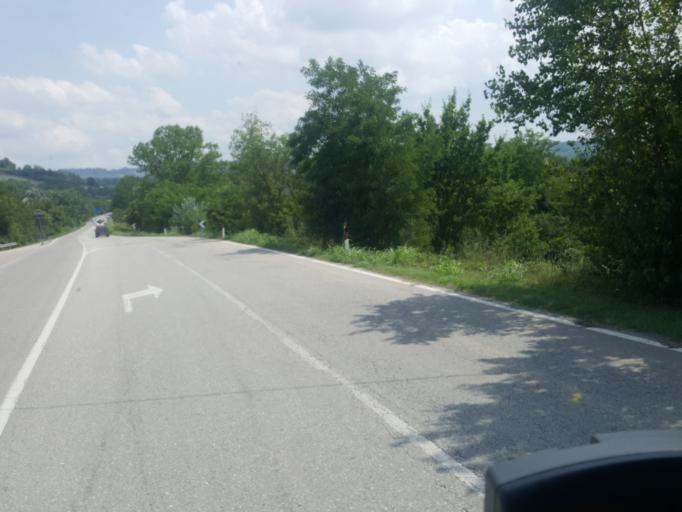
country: IT
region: Piedmont
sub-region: Provincia di Cuneo
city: Monchiero Borgonuovo
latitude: 44.5846
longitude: 7.9029
